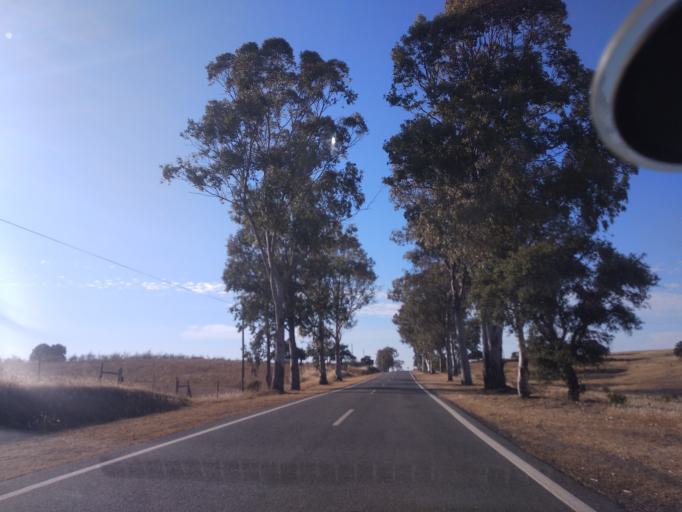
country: PT
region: Beja
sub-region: Almodovar
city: Almodovar
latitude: 37.4452
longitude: -7.9953
